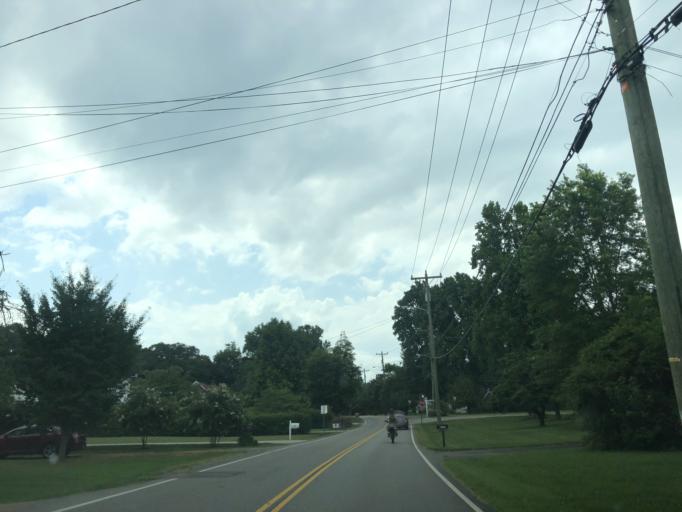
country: US
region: Tennessee
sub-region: Davidson County
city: Lakewood
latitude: 36.1678
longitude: -86.6692
